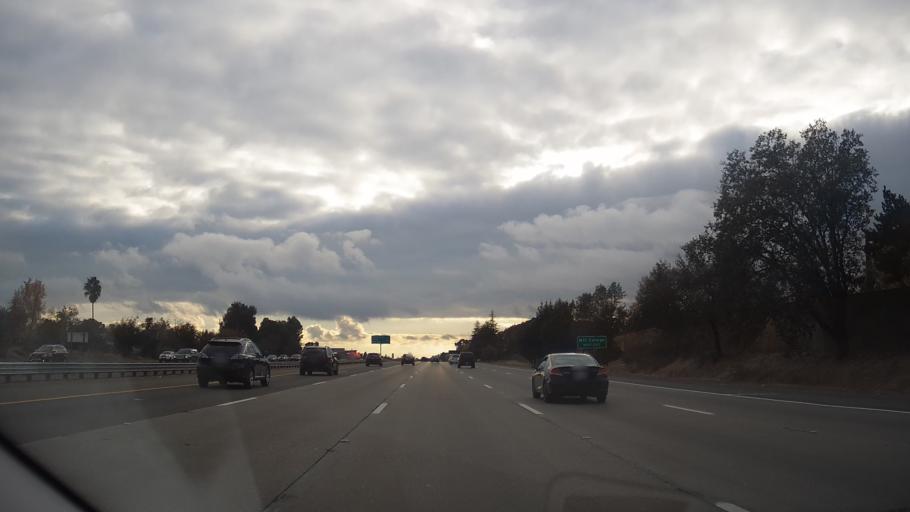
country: US
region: California
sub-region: Sacramento County
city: Foothill Farms
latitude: 38.6713
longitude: -121.3495
